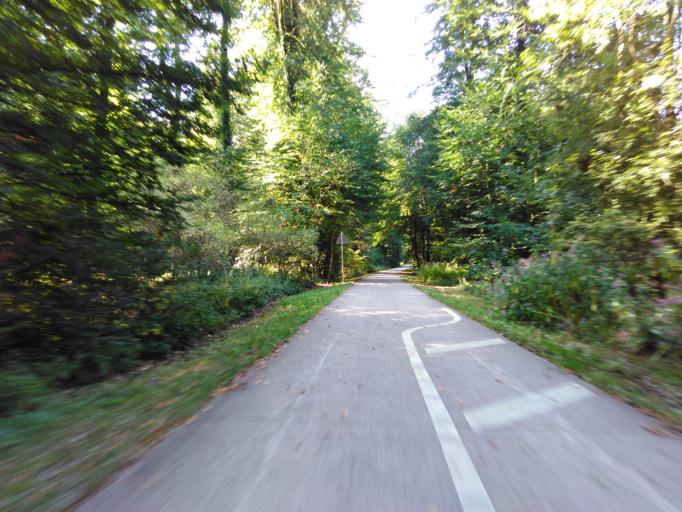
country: LU
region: Luxembourg
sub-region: Canton de Capellen
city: Hobscheid
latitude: 49.6735
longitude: 5.9068
